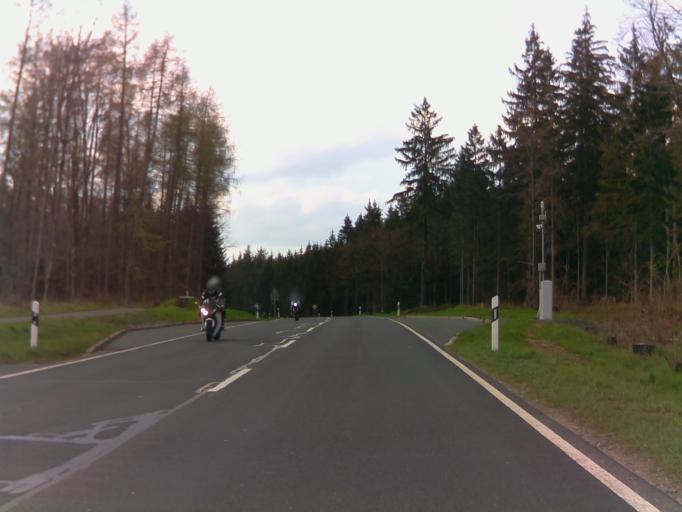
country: DE
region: Bavaria
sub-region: Upper Franconia
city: Ludwigsstadt
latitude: 50.4579
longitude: 11.3463
